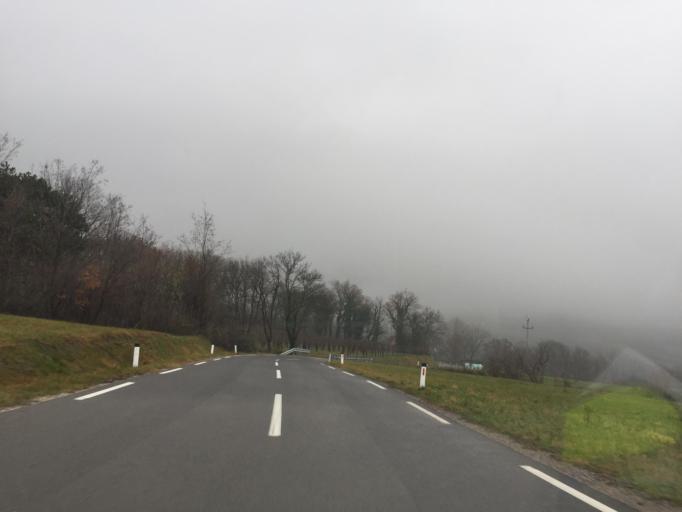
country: SI
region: Ajdovscina
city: Lokavec
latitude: 45.9047
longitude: 13.8857
